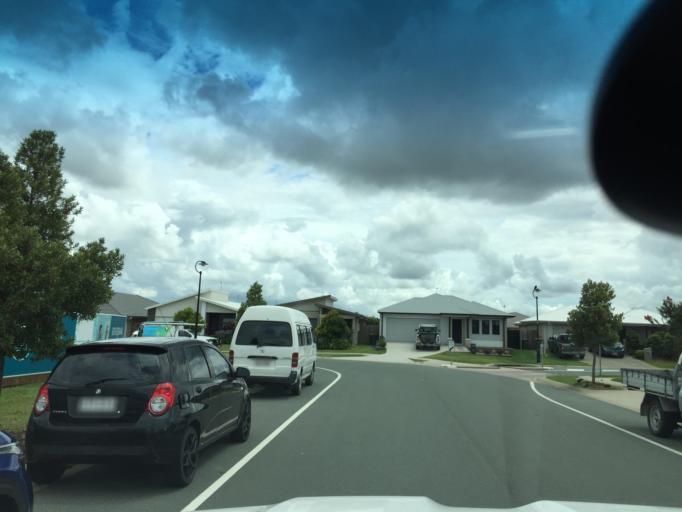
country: AU
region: Queensland
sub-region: Moreton Bay
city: Caboolture South
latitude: -27.0951
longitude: 152.9647
